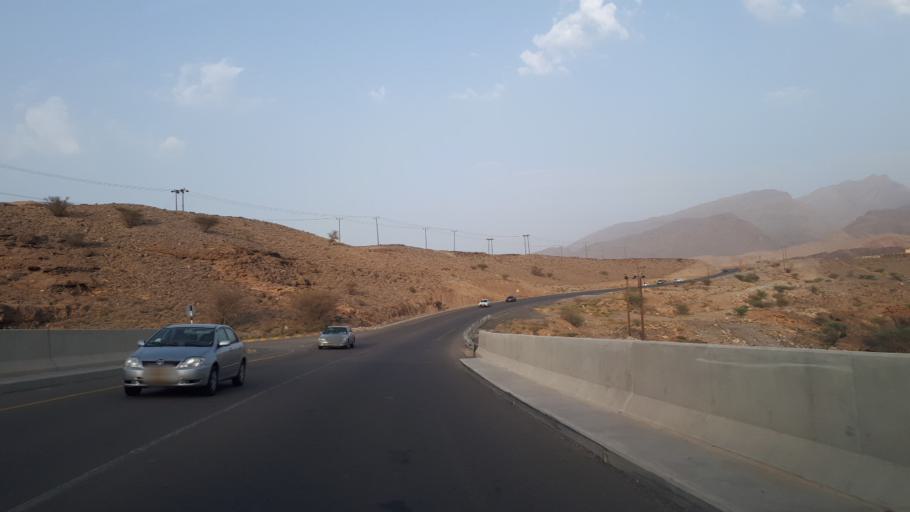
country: OM
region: Al Batinah
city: Rustaq
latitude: 23.3900
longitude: 57.2196
